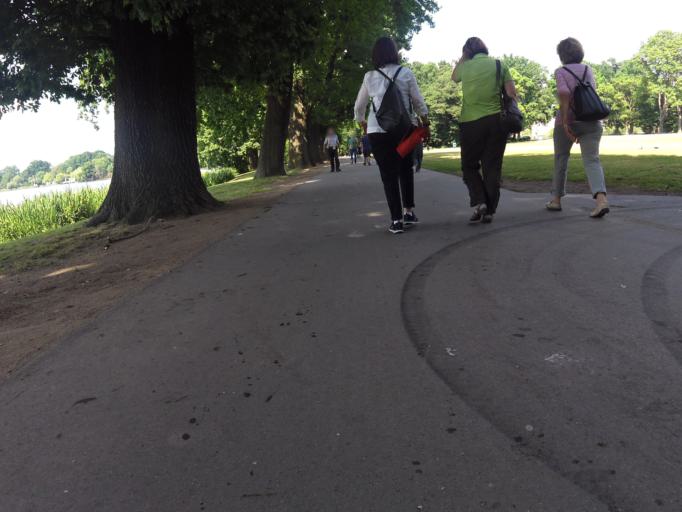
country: DE
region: Bavaria
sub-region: Regierungsbezirk Mittelfranken
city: Nuernberg
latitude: 49.4289
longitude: 11.1181
